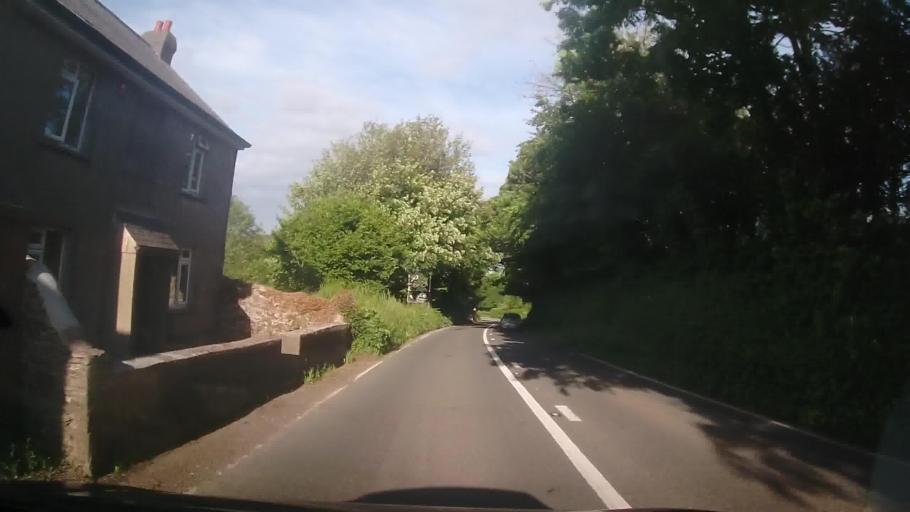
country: GB
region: England
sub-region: Devon
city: Ivybridge
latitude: 50.3526
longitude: -3.9333
